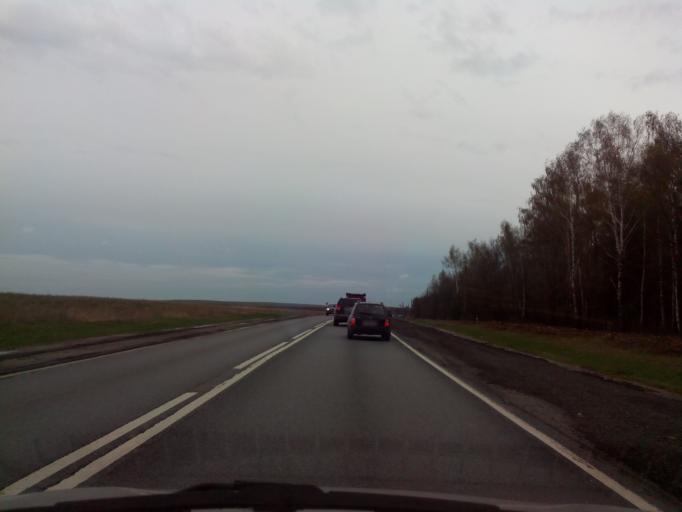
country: RU
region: Moskovskaya
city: Ozherel'ye
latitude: 54.6939
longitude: 38.3142
